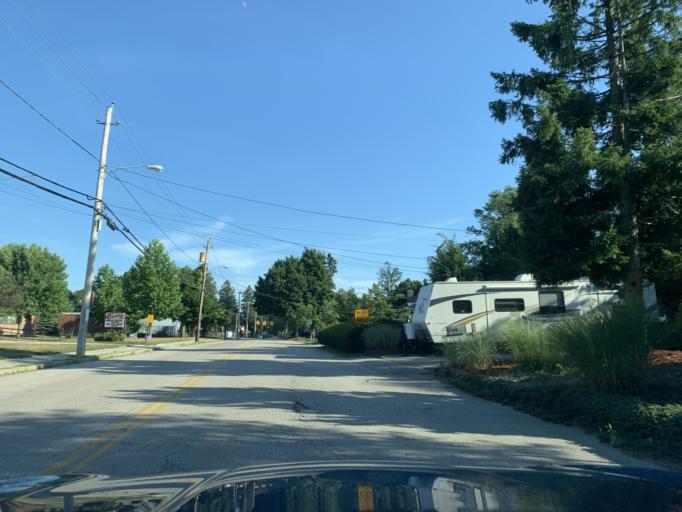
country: US
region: Rhode Island
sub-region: Kent County
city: Warwick
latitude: 41.6991
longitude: -71.4409
